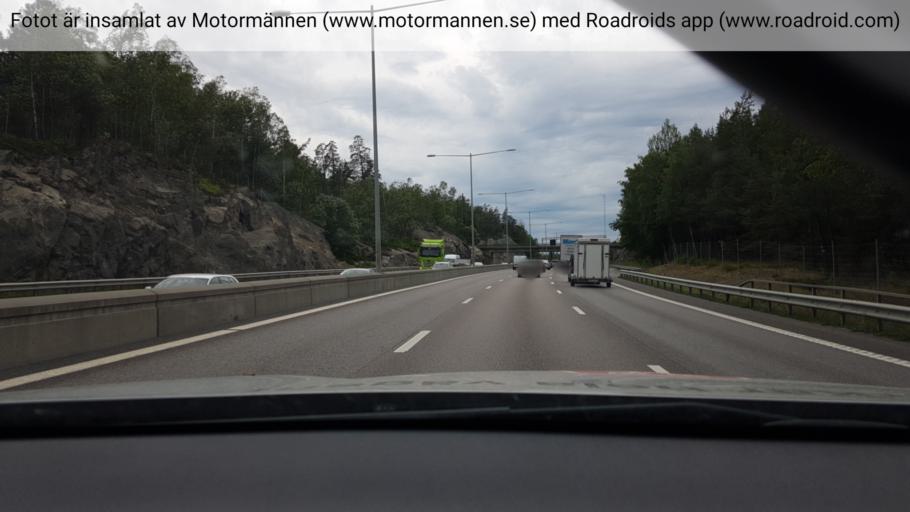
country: SE
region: Stockholm
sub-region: Salems Kommun
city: Ronninge
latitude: 59.2067
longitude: 17.6977
